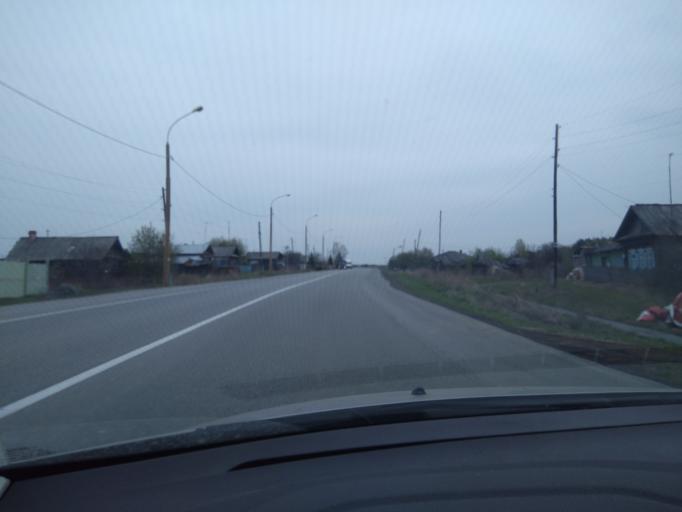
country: RU
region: Sverdlovsk
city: Beloyarskiy
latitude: 56.7707
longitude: 61.4670
